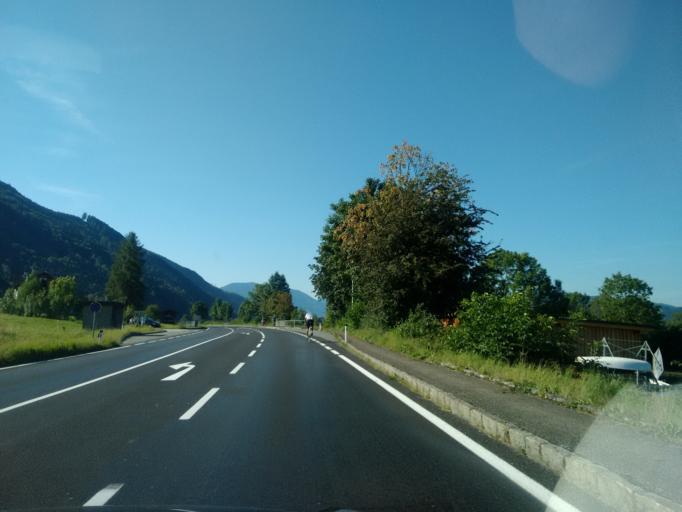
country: AT
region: Upper Austria
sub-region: Politischer Bezirk Vocklabruck
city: Attersee
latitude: 47.8766
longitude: 13.5681
